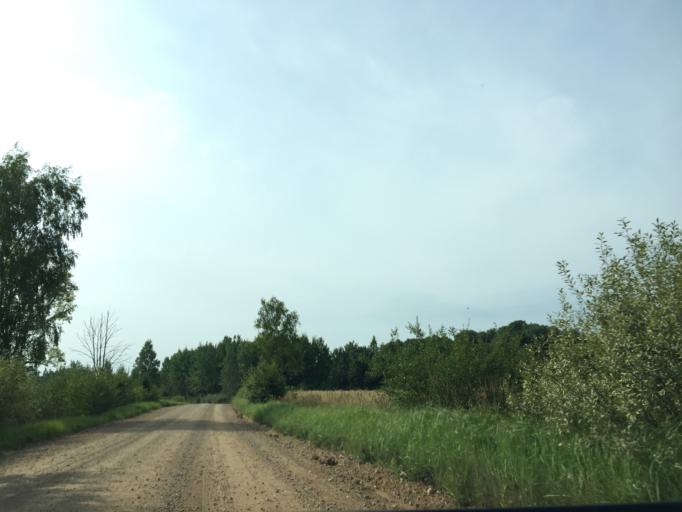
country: LV
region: Ludzas Rajons
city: Ludza
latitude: 56.3188
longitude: 27.7666
